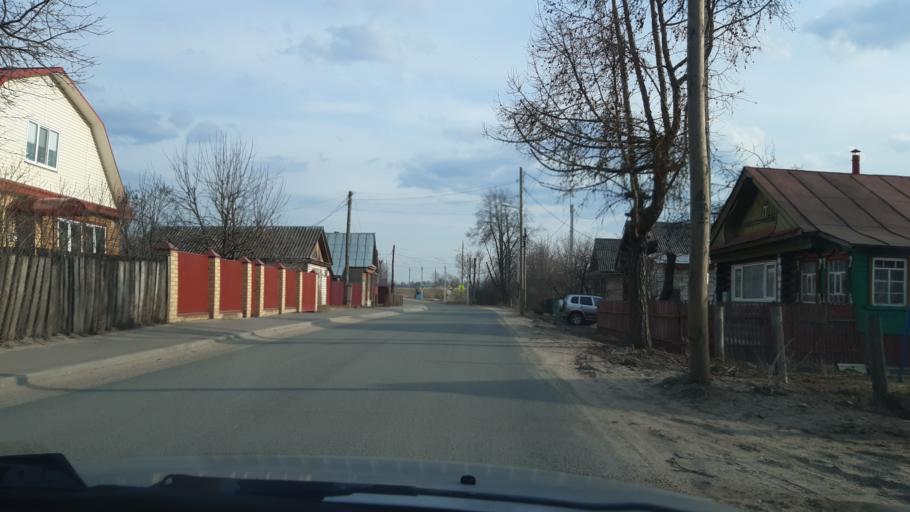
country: RU
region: Vladimir
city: Nikologory
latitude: 56.1364
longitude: 41.9919
